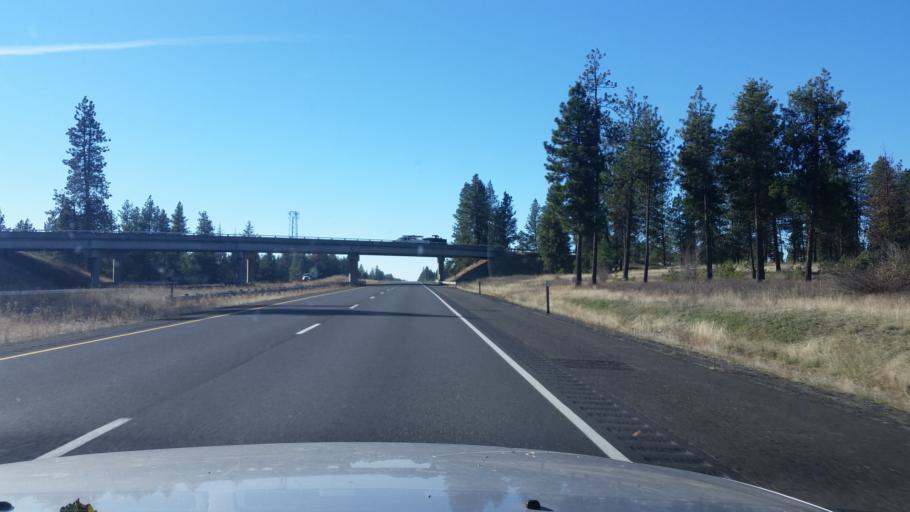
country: US
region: Washington
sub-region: Spokane County
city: Medical Lake
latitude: 47.5054
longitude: -117.6898
